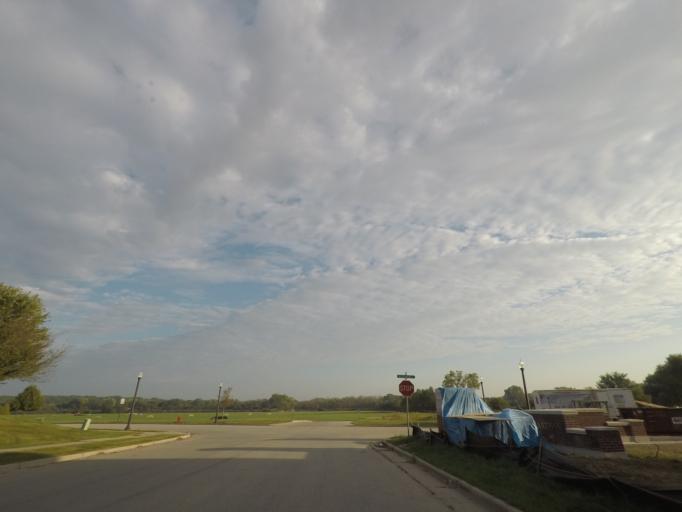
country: US
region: Wisconsin
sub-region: Waukesha County
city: Brookfield
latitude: 43.0386
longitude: -88.1110
